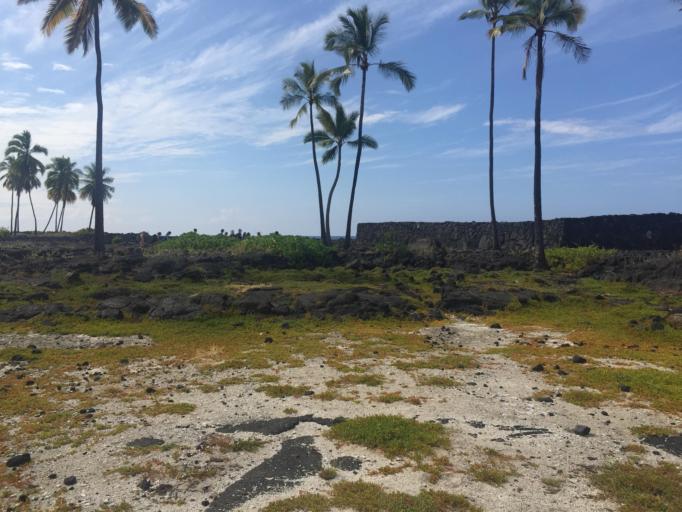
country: US
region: Hawaii
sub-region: Hawaii County
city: Honaunau-Napoopoo
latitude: 19.4208
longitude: -155.9121
